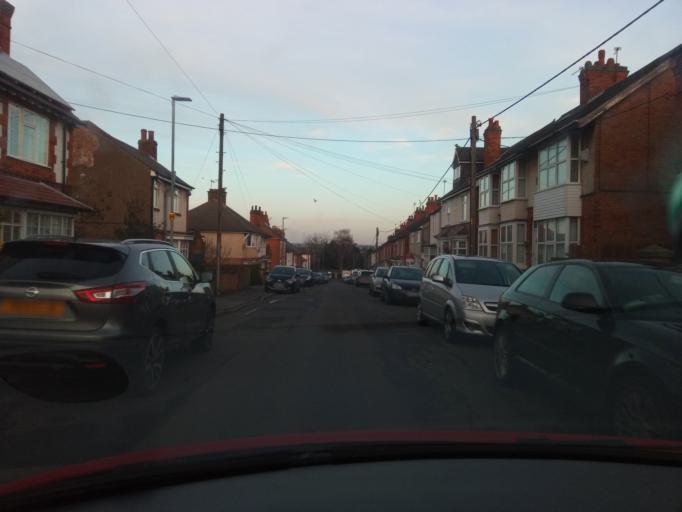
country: GB
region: England
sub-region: Leicestershire
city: Mountsorrel
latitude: 52.7235
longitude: -1.1377
